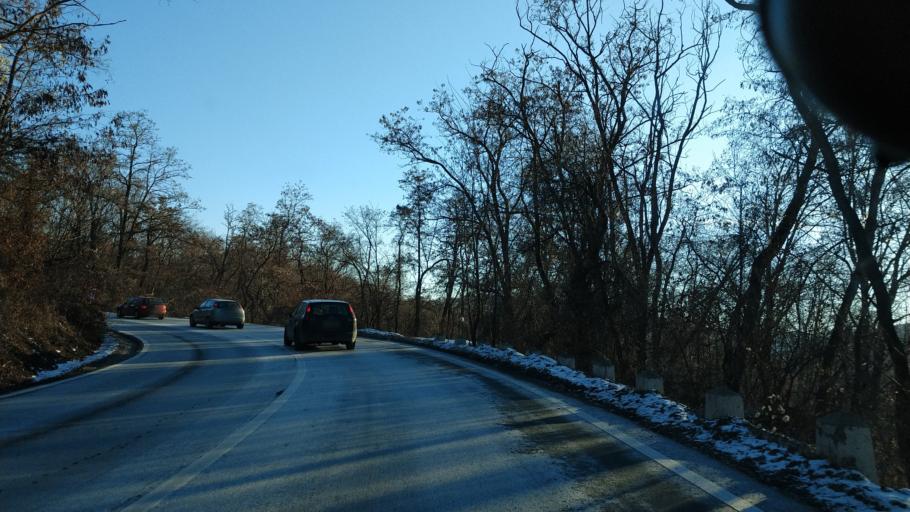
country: RO
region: Bacau
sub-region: Comuna Luizi-Calugara
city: Luizi-Calugara
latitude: 46.5324
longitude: 26.8223
